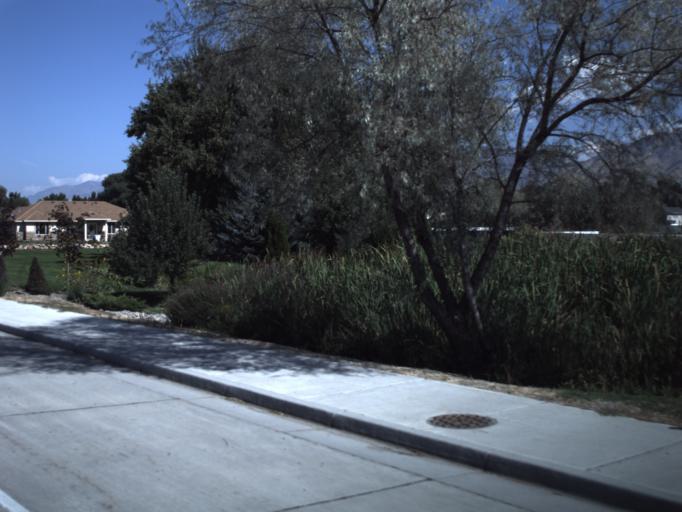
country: US
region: Utah
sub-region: Cache County
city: Logan
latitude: 41.7141
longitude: -111.8601
